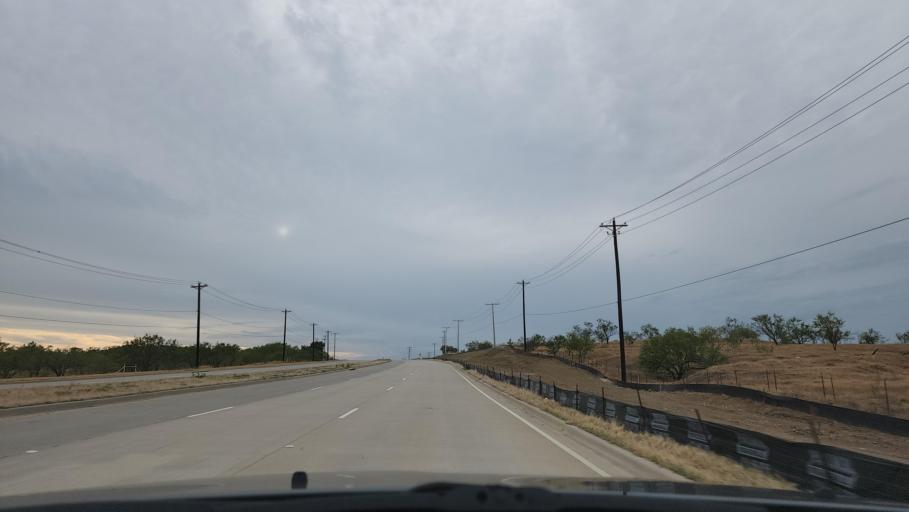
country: US
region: Texas
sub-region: Denton County
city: Roanoke
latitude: 33.0637
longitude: -97.2275
